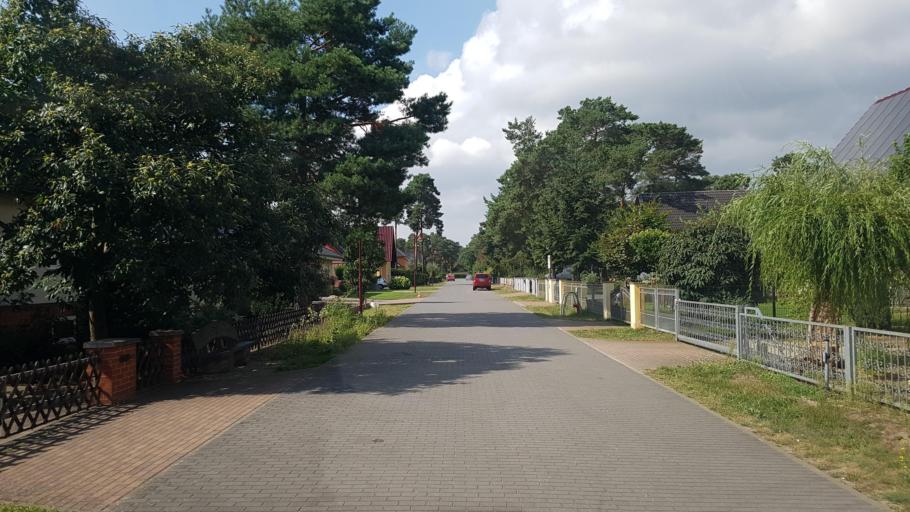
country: DE
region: Brandenburg
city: Bruck
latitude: 52.1838
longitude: 12.7632
